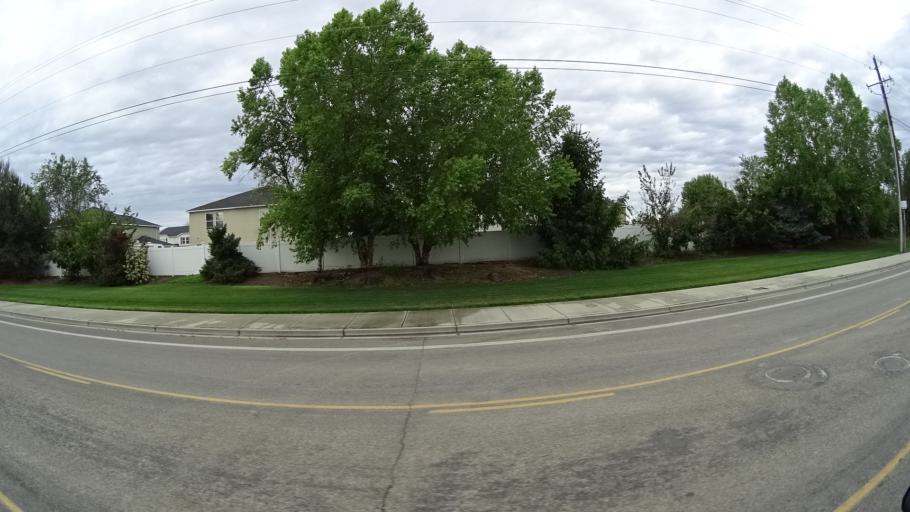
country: US
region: Idaho
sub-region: Ada County
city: Star
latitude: 43.7041
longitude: -116.4933
